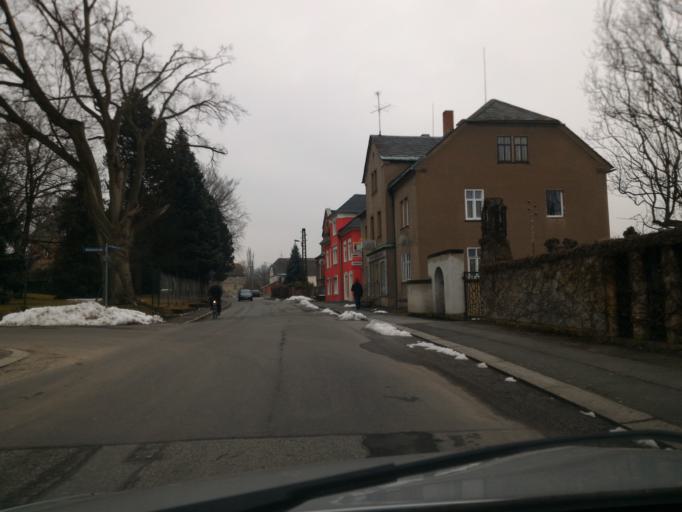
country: DE
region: Saxony
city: Neugersdorf
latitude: 50.9834
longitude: 14.6036
